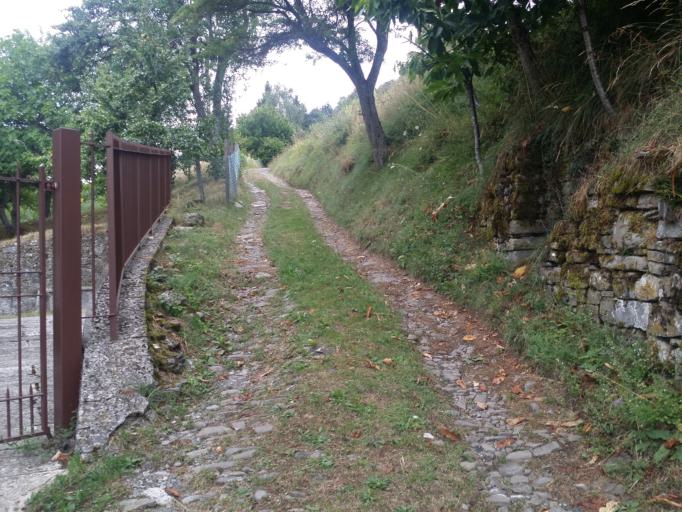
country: IT
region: Emilia-Romagna
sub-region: Provincia di Parma
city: Borgo Val di Taro
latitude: 44.5322
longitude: 9.7919
